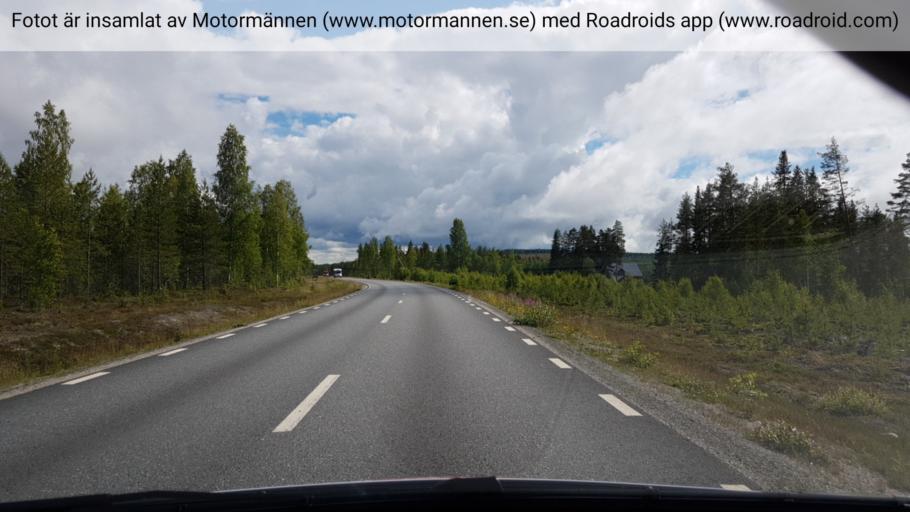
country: SE
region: Vaesterbotten
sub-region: Bjurholms Kommun
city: Bjurholm
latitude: 64.2965
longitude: 19.1786
